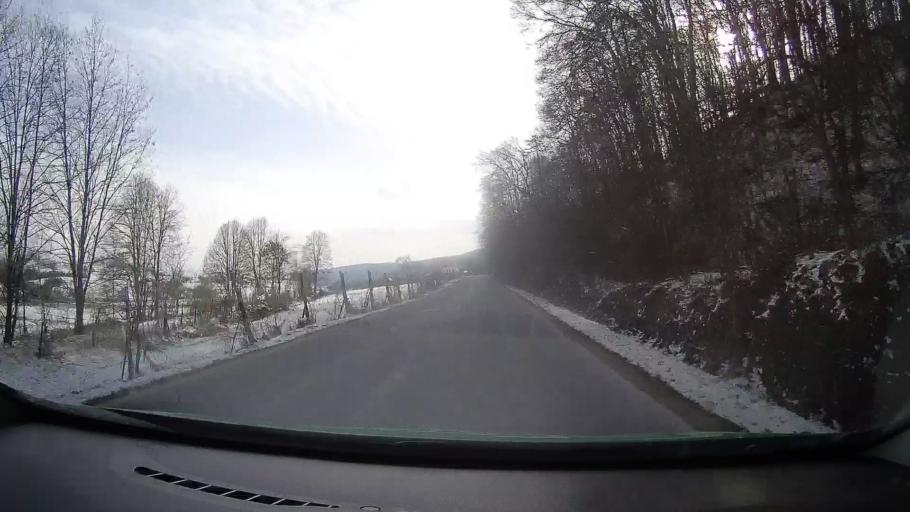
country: RO
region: Mures
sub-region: Comuna Apold
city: Saes
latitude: 46.1774
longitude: 24.7574
